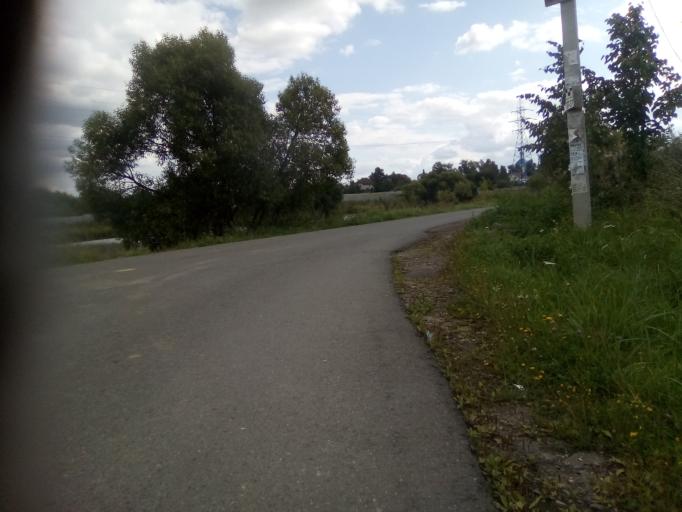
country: RU
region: Moskovskaya
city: Zhavoronki
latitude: 55.6597
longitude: 37.1354
